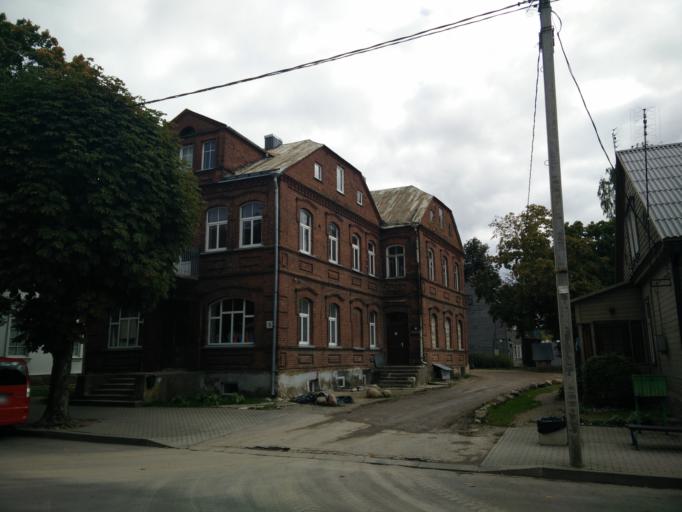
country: LT
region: Utenos apskritis
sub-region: Anyksciai
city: Anyksciai
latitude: 55.5244
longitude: 25.1024
